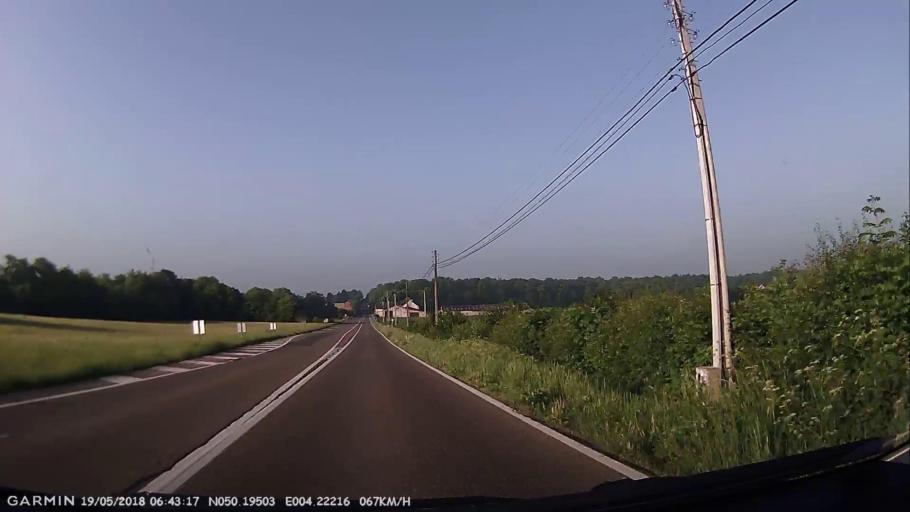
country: BE
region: Wallonia
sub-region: Province du Hainaut
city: Beaumont
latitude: 50.1948
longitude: 4.2221
